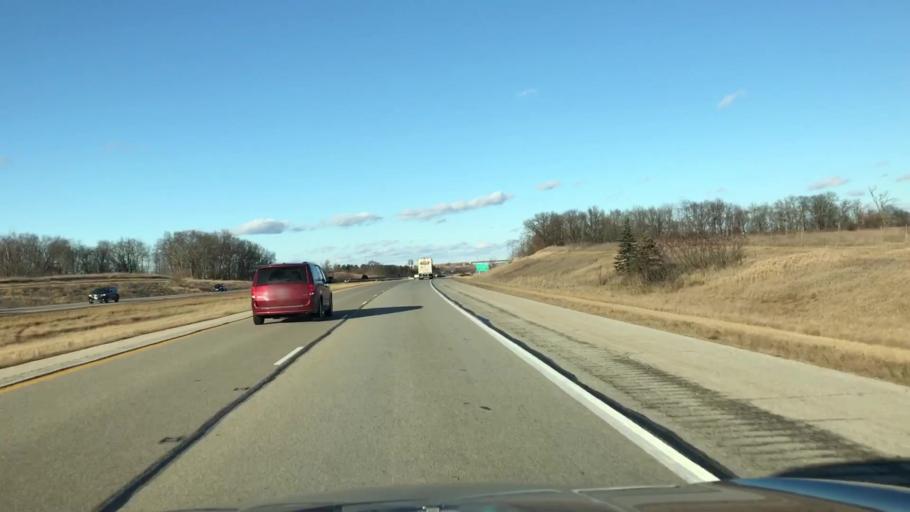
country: US
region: Illinois
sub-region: McLean County
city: Lexington
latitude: 40.6321
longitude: -88.8153
